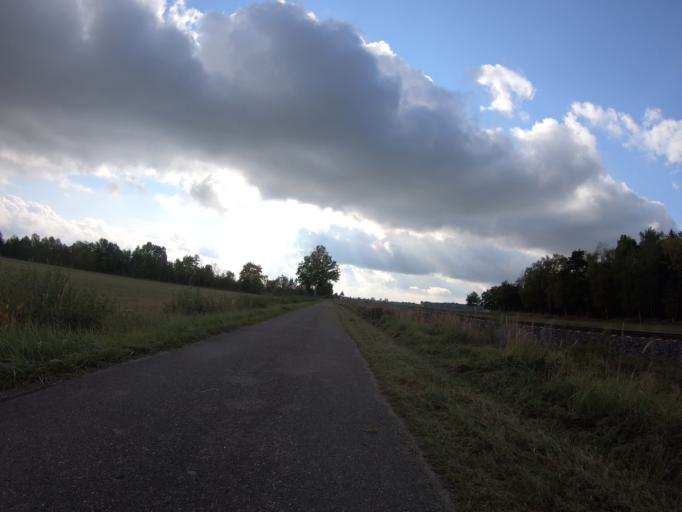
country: DE
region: Lower Saxony
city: Wahrenholz
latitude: 52.5879
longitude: 10.6095
